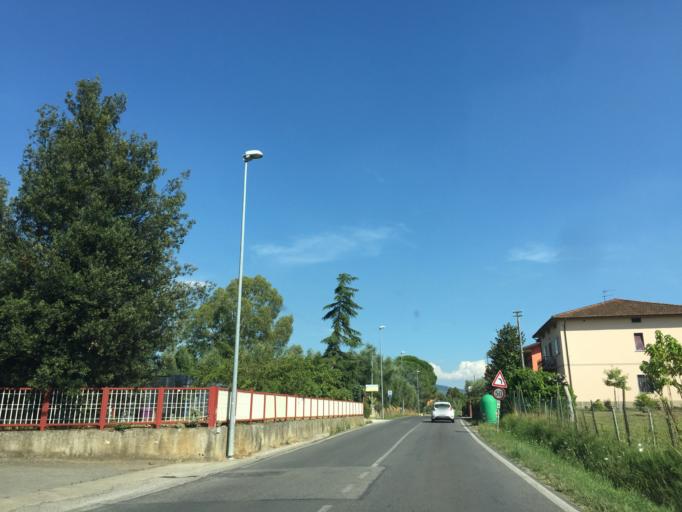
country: IT
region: Tuscany
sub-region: Provincia di Pistoia
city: San Rocco
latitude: 43.8306
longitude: 10.8553
